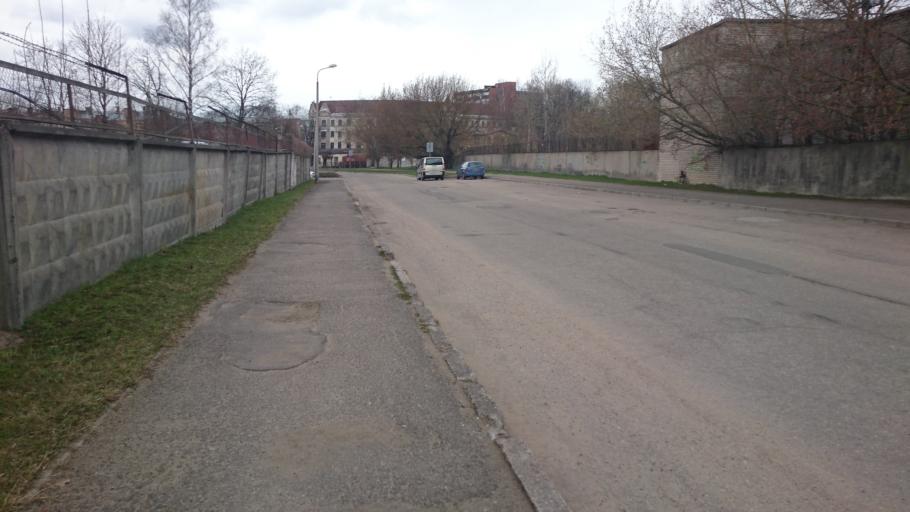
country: LV
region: Riga
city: Riga
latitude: 56.9577
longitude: 24.0741
